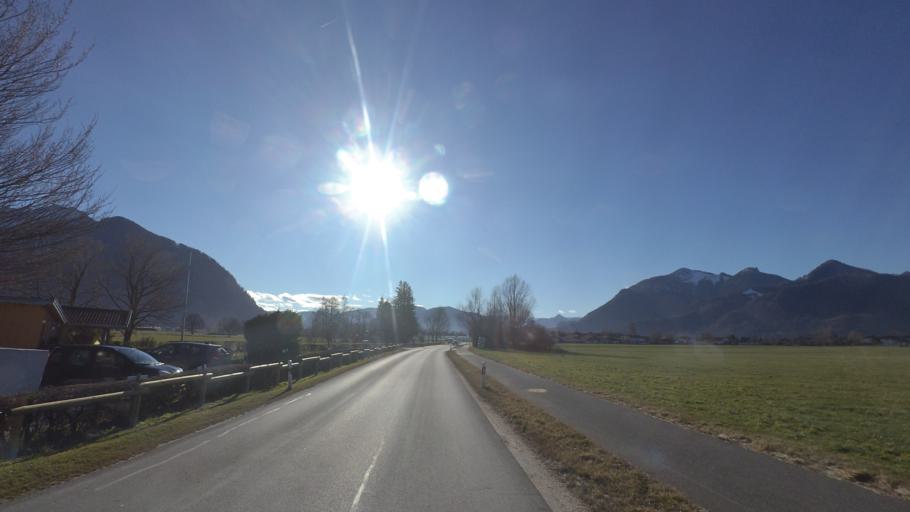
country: DE
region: Bavaria
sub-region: Upper Bavaria
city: Staudach-Egerndach
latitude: 47.7906
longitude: 12.4697
